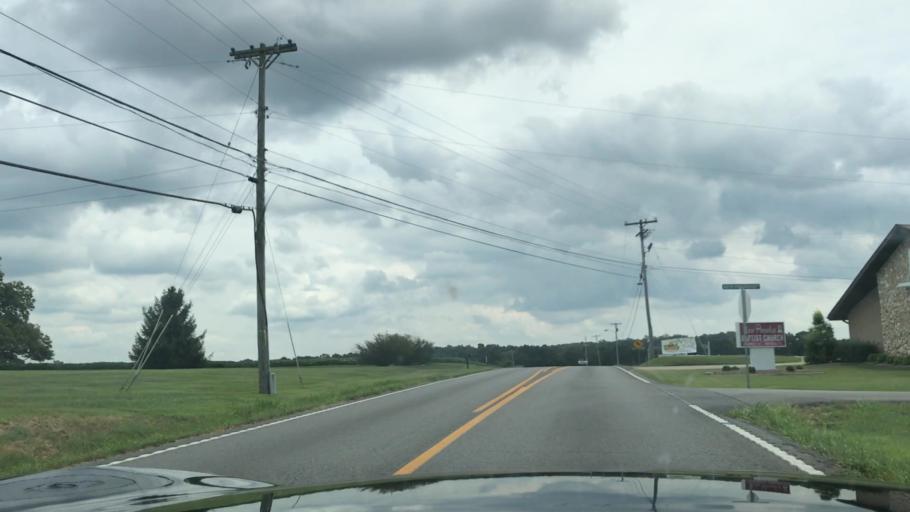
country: US
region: Kentucky
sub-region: Muhlenberg County
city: Greenville
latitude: 37.1990
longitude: -87.1322
